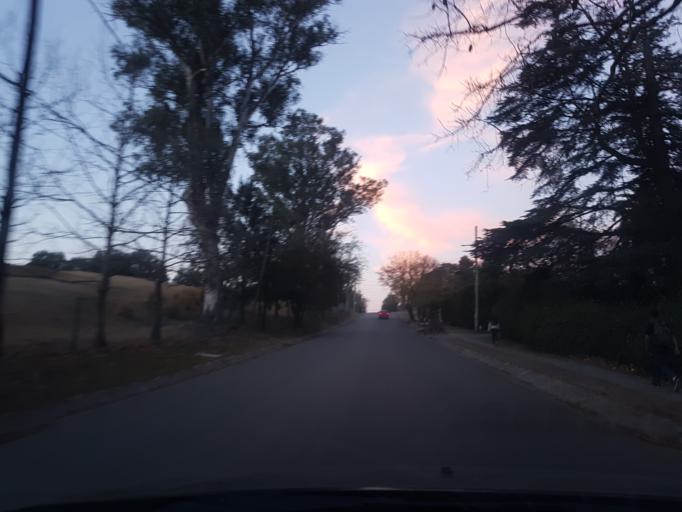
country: AR
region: Cordoba
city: Villa Allende
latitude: -31.2852
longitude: -64.2930
